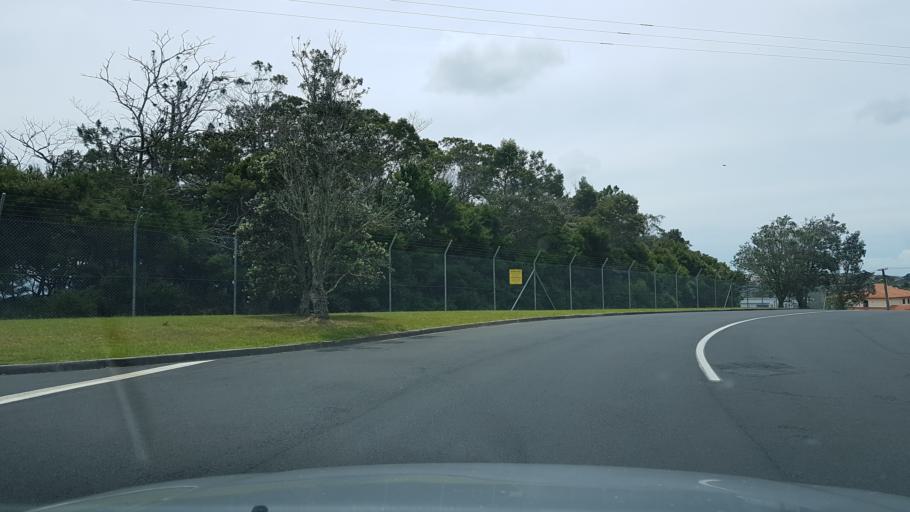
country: NZ
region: Auckland
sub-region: Auckland
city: North Shore
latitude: -36.8196
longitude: 174.7078
